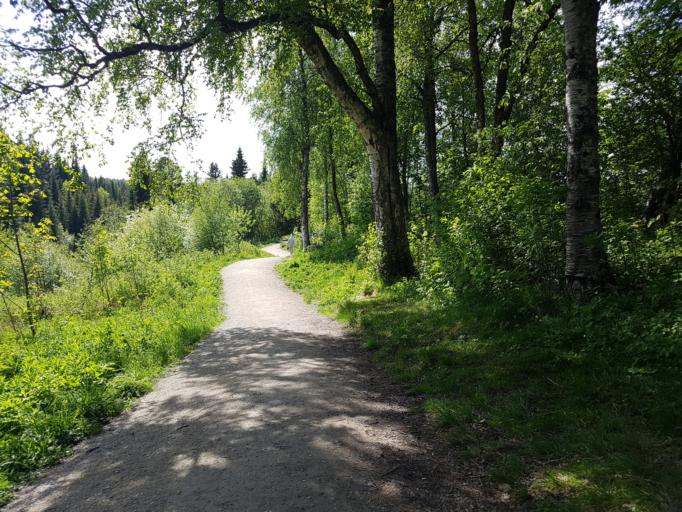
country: NO
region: Sor-Trondelag
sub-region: Trondheim
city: Trondheim
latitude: 63.4205
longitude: 10.3413
